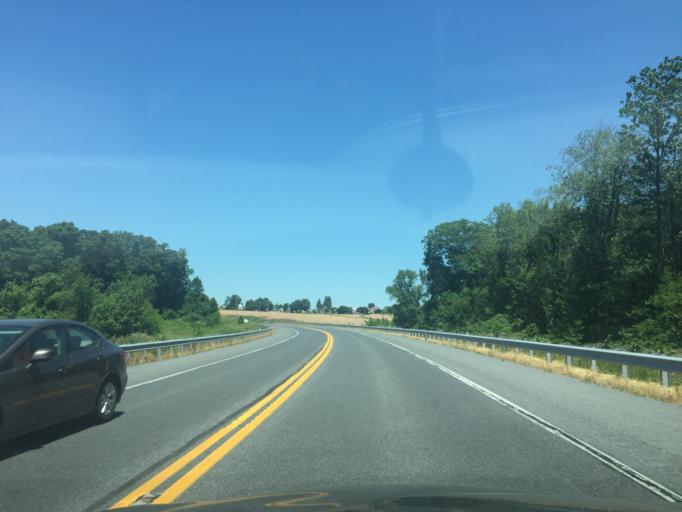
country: US
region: Maryland
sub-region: Carroll County
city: Hampstead
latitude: 39.5911
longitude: -76.8540
